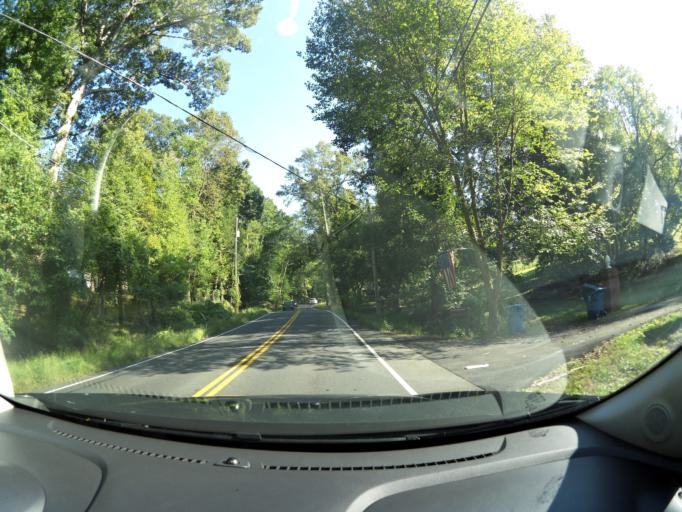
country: US
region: Virginia
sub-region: Fairfax County
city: Great Falls
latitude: 38.9736
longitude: -77.2438
